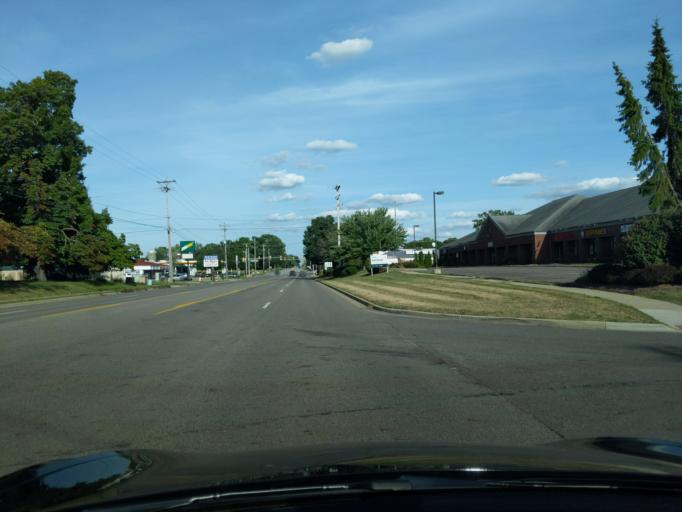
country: US
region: Michigan
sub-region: Eaton County
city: Waverly
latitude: 42.7265
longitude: -84.6447
